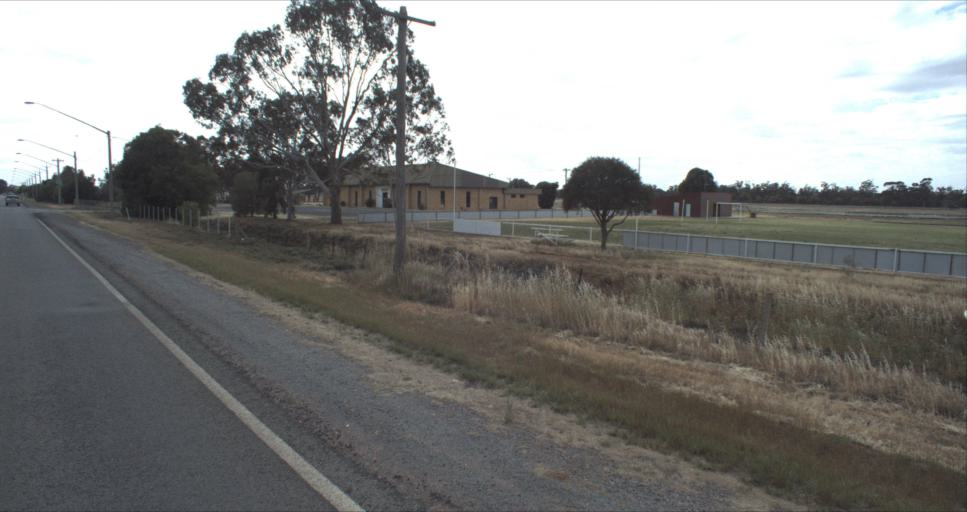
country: AU
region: New South Wales
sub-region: Leeton
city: Leeton
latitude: -34.5637
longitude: 146.3991
